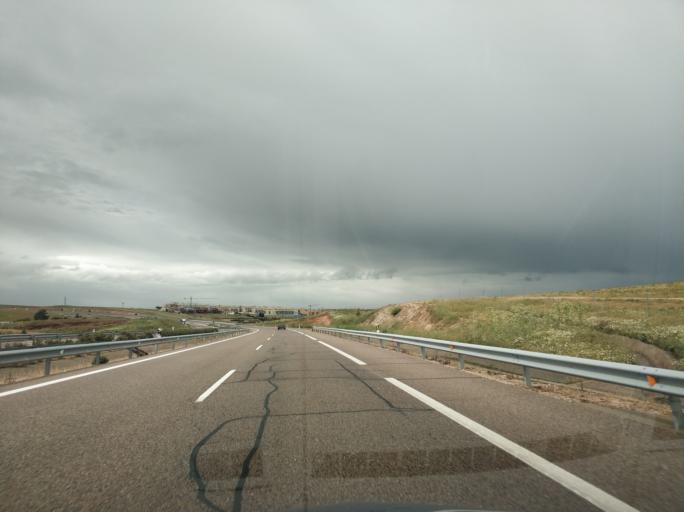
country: ES
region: Castille and Leon
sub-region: Provincia de Salamanca
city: Aldeatejada
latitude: 40.9349
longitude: -5.6799
